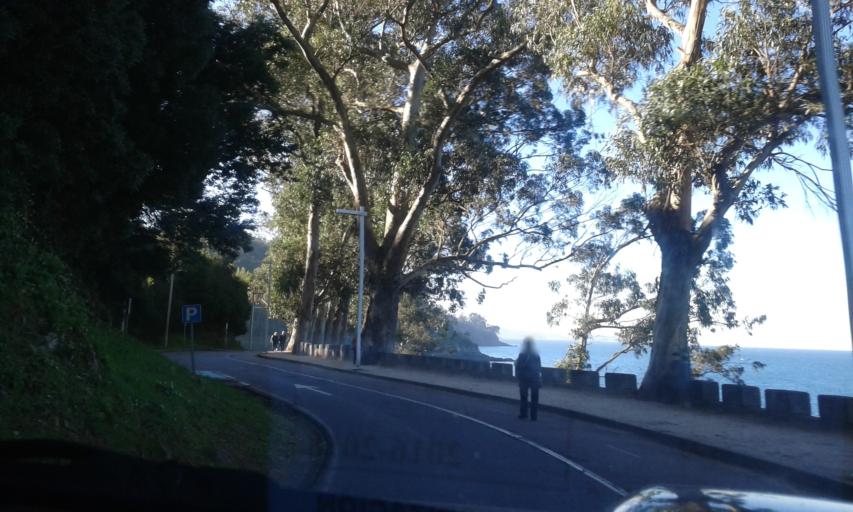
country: ES
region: Galicia
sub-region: Provincia de Pontevedra
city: Marin
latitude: 42.3923
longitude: -8.7135
